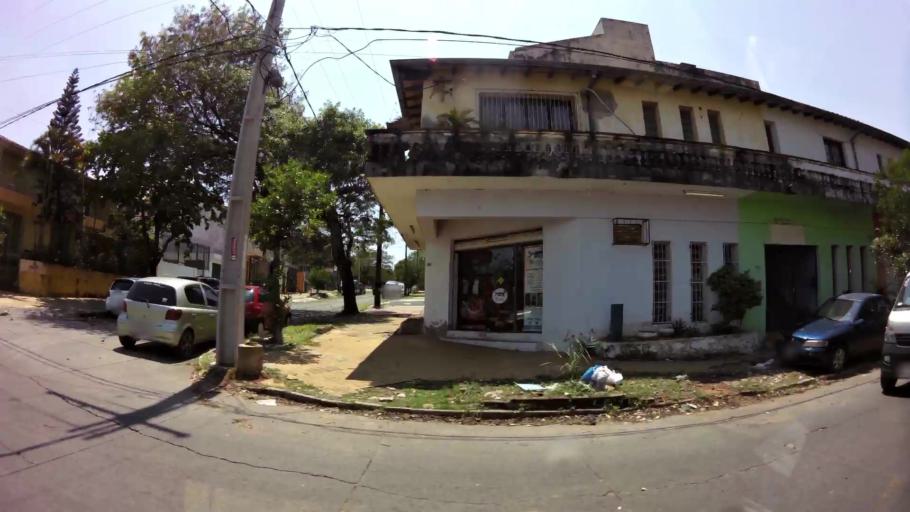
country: PY
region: Asuncion
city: Asuncion
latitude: -25.2966
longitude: -57.6554
